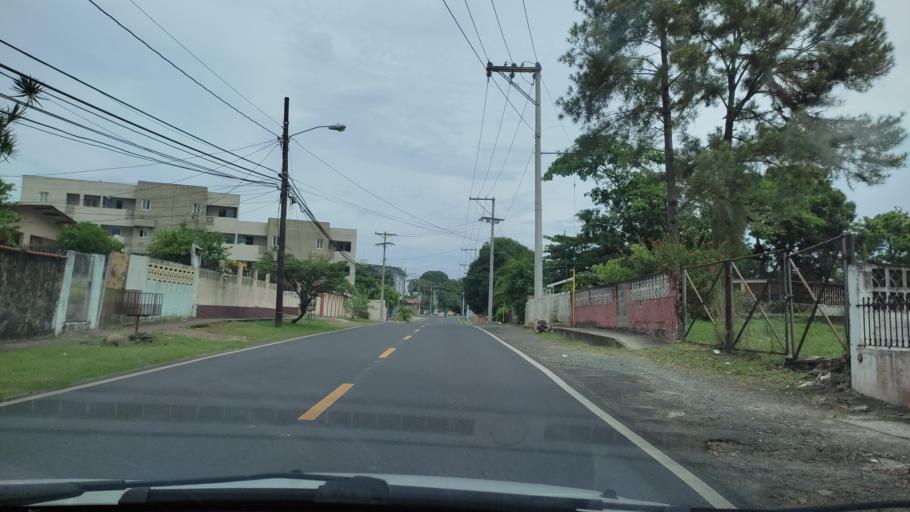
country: PA
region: Panama
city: San Miguelito
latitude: 9.0451
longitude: -79.4308
